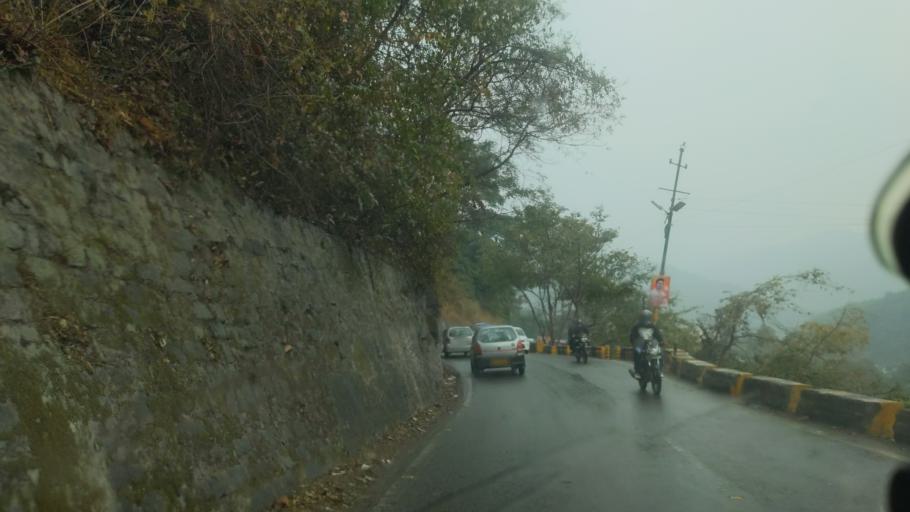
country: IN
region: Uttarakhand
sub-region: Naini Tal
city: Haldwani
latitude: 29.2788
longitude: 79.5448
